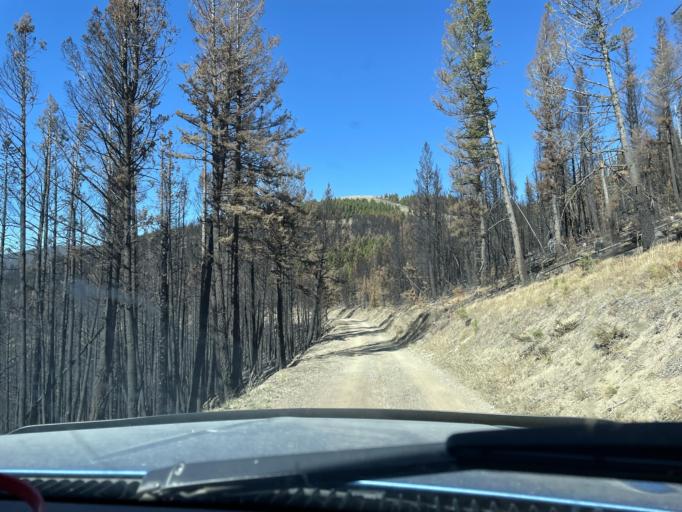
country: US
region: Montana
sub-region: Broadwater County
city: Townsend
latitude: 46.5055
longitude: -111.2754
